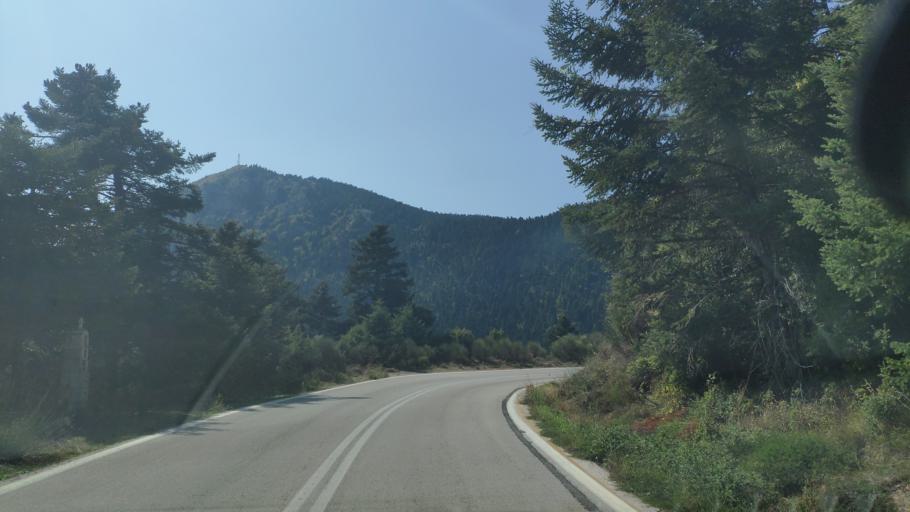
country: GR
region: West Greece
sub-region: Nomos Achaias
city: Aiyira
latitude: 37.8658
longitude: 22.3734
